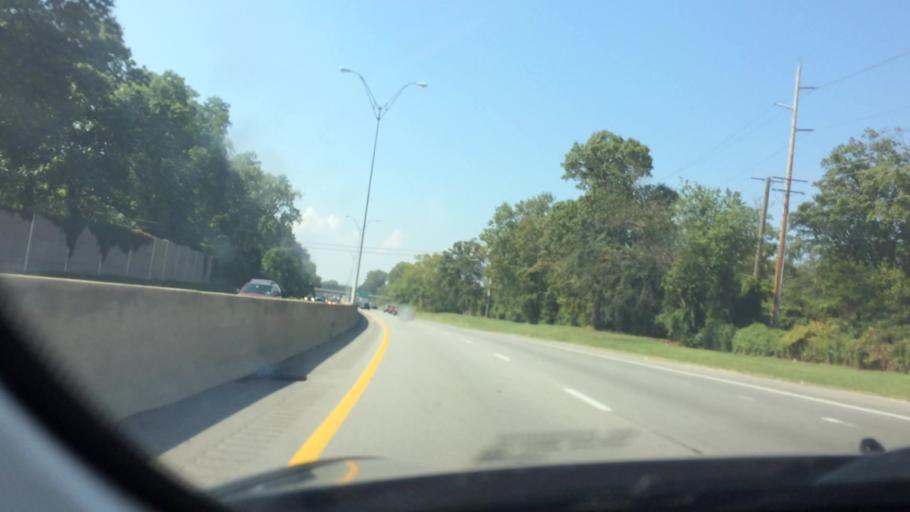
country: US
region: Ohio
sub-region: Lucas County
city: Ottawa Hills
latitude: 41.6884
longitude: -83.6292
